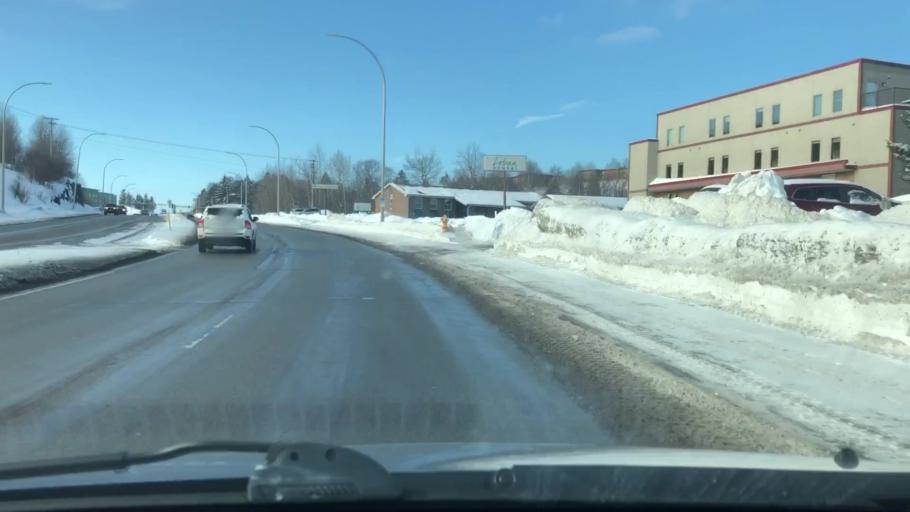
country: US
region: Minnesota
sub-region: Saint Louis County
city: Duluth
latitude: 46.7992
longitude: -92.1119
